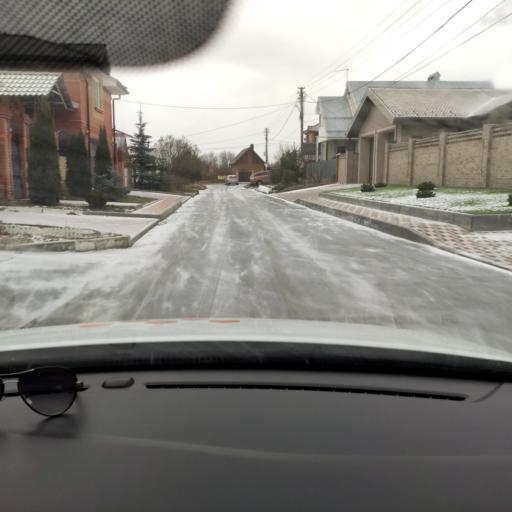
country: RU
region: Tatarstan
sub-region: Gorod Kazan'
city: Kazan
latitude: 55.8190
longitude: 49.2250
